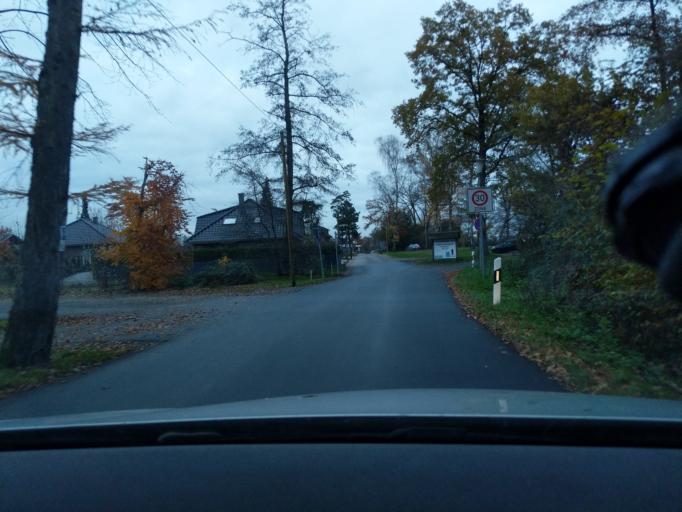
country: DE
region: North Rhine-Westphalia
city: Selm
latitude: 51.7120
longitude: 7.4270
